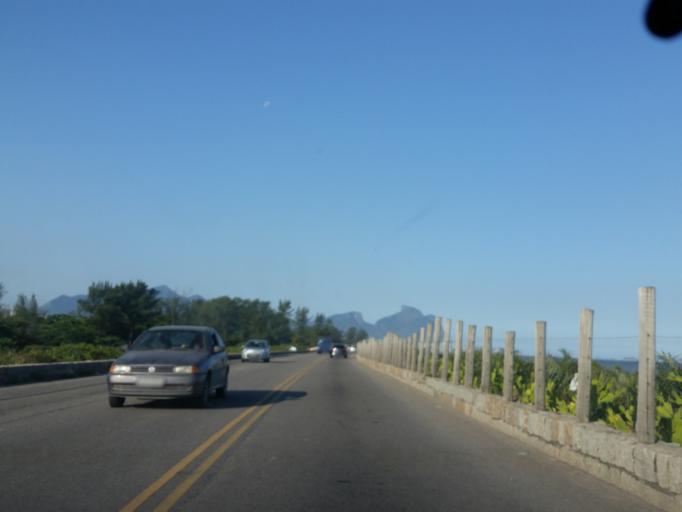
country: BR
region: Rio de Janeiro
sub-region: Nilopolis
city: Nilopolis
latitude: -23.0178
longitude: -43.4250
